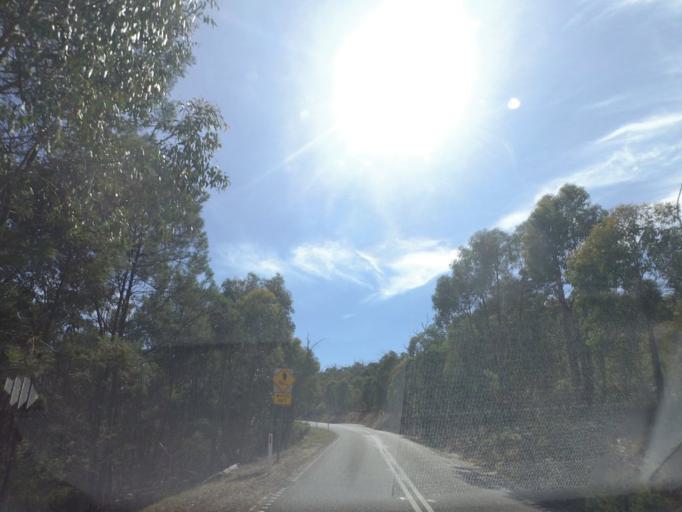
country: AU
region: Victoria
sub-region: Nillumbik
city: Saint Andrews
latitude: -37.5673
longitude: 145.3062
